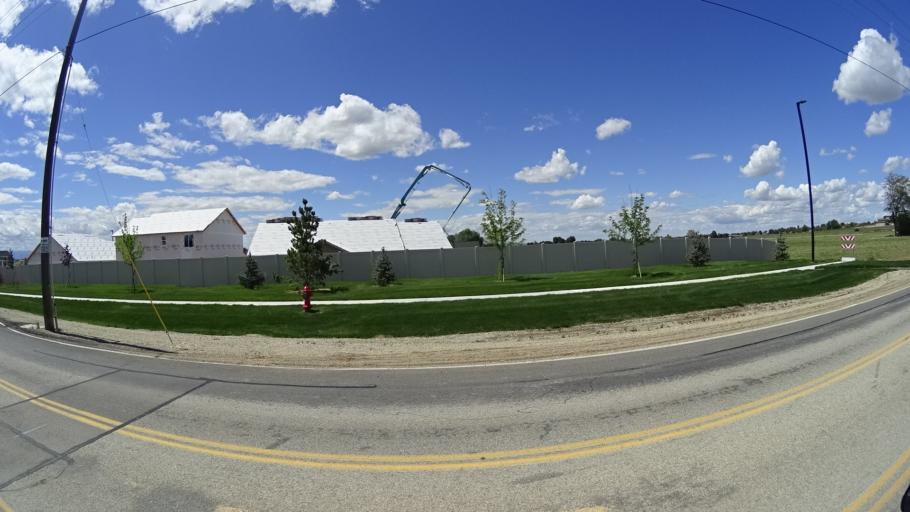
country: US
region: Idaho
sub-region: Ada County
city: Kuna
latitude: 43.5518
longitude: -116.4338
